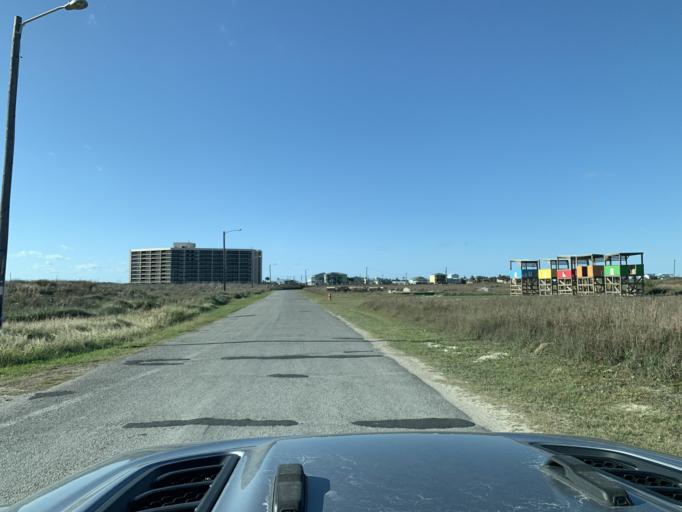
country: US
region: Texas
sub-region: Nueces County
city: Port Aransas
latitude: 27.8307
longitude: -97.0527
